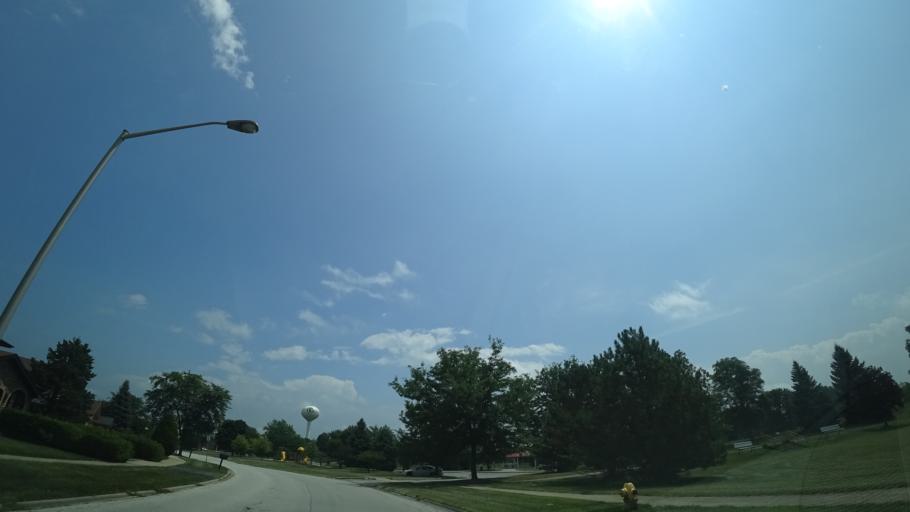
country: US
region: Illinois
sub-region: Cook County
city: Matteson
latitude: 41.5250
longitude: -87.7538
